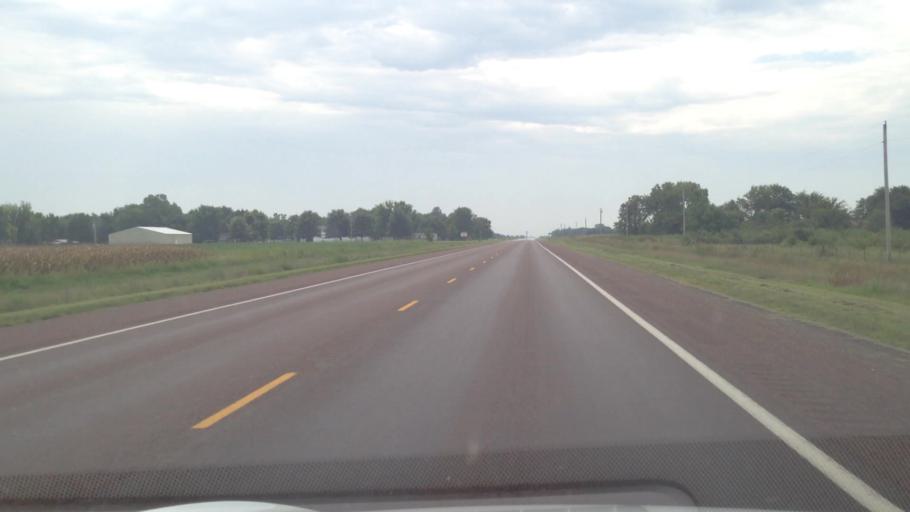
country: US
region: Kansas
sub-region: Crawford County
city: Girard
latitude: 37.4433
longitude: -94.8330
